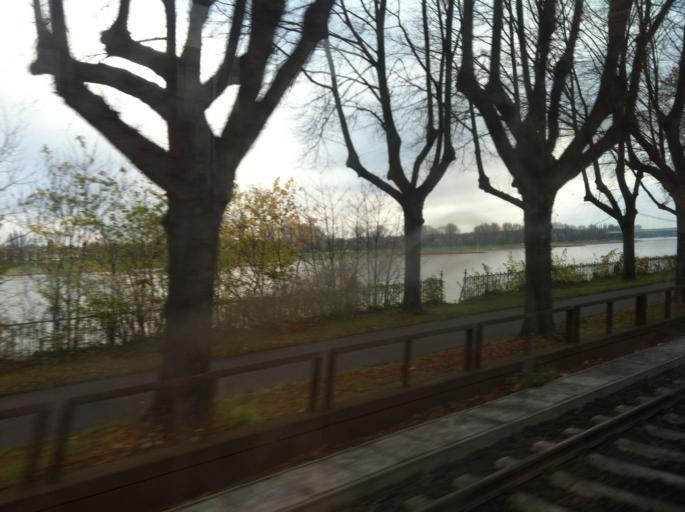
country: DE
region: North Rhine-Westphalia
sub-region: Regierungsbezirk Koln
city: Bayenthal
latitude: 50.9093
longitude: 6.9756
